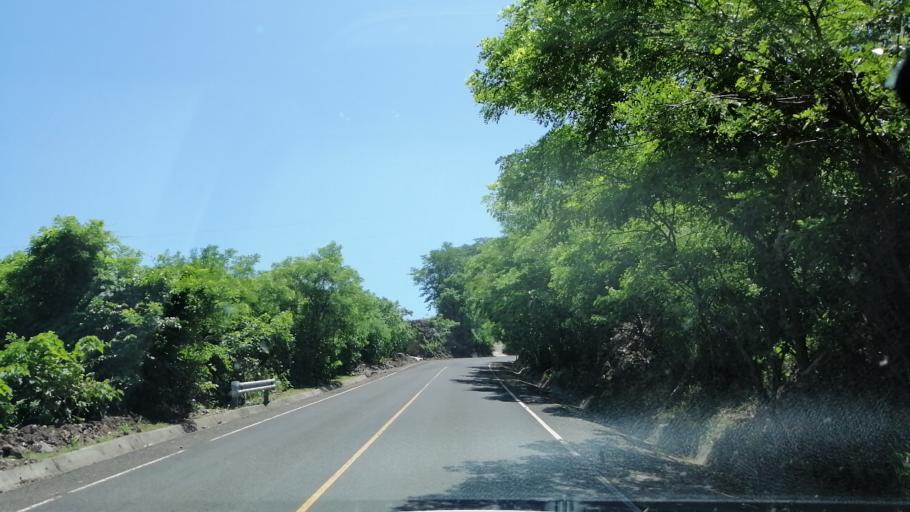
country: SV
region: San Miguel
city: Sesori
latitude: 13.8078
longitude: -88.4006
